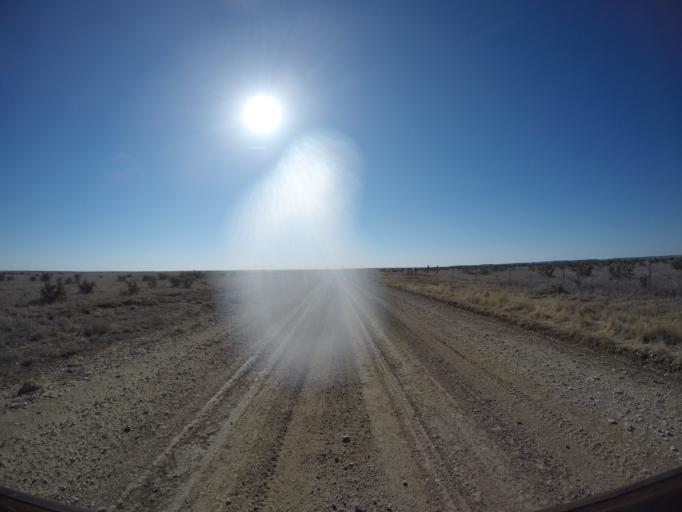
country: US
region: Colorado
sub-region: Otero County
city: La Junta
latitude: 37.6807
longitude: -103.6204
